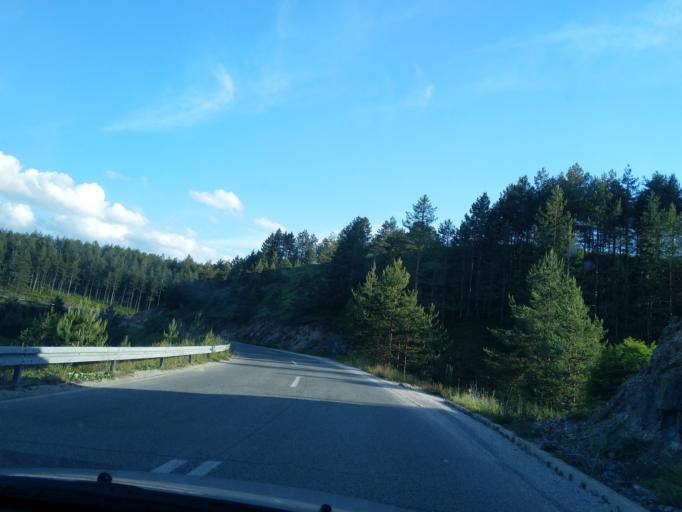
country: RS
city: Zlatibor
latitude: 43.6923
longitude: 19.6621
